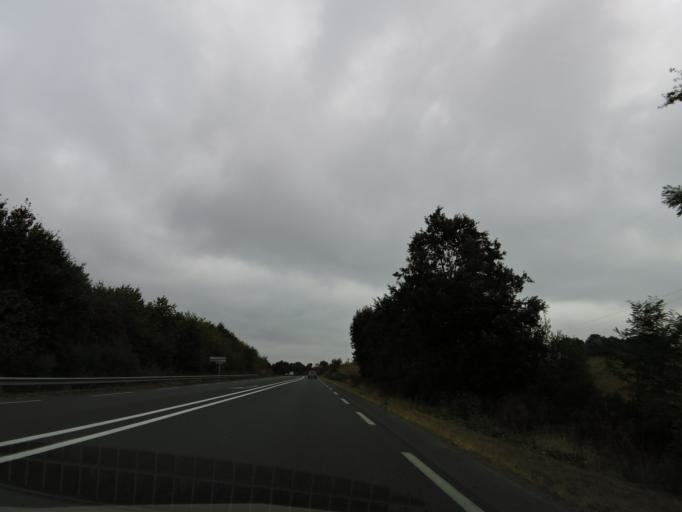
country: FR
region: Pays de la Loire
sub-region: Departement de la Vendee
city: Aubigny
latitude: 46.5976
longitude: -1.4426
